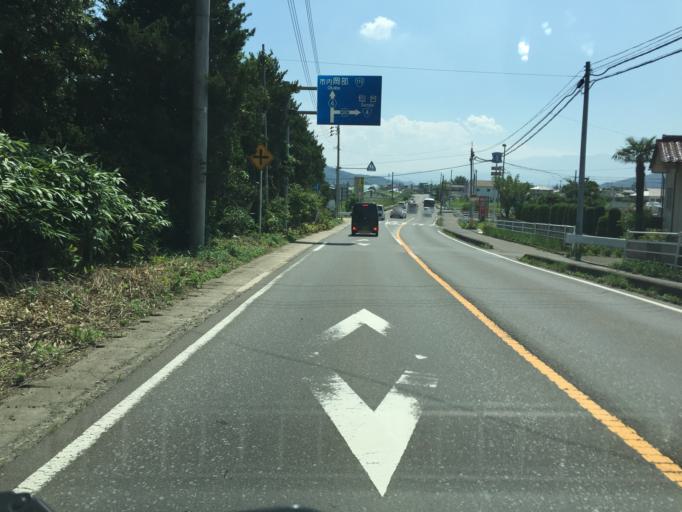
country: JP
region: Fukushima
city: Hobaramachi
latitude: 37.7946
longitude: 140.5161
